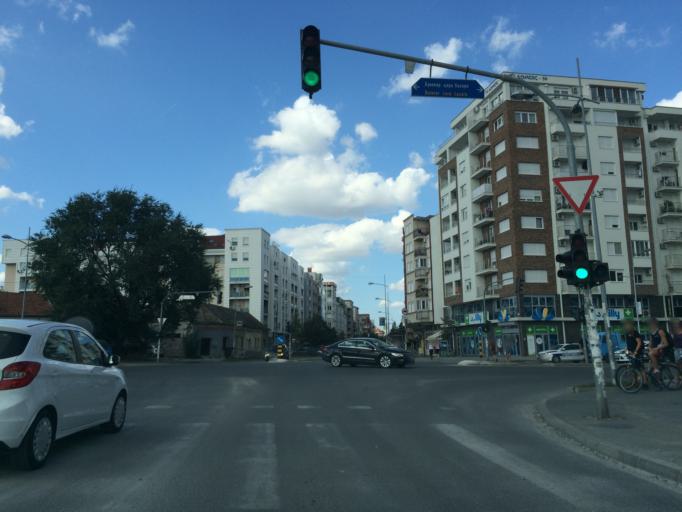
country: RS
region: Autonomna Pokrajina Vojvodina
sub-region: Juznobacki Okrug
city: Novi Sad
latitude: 45.2395
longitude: 19.8256
